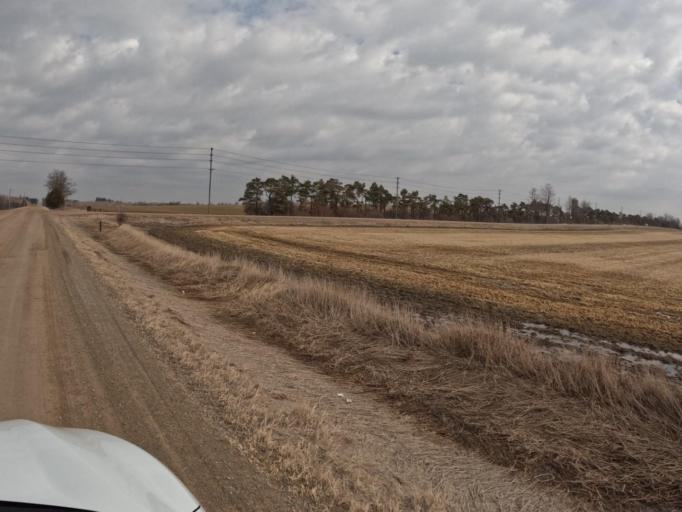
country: CA
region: Ontario
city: Orangeville
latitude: 43.9282
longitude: -80.1873
